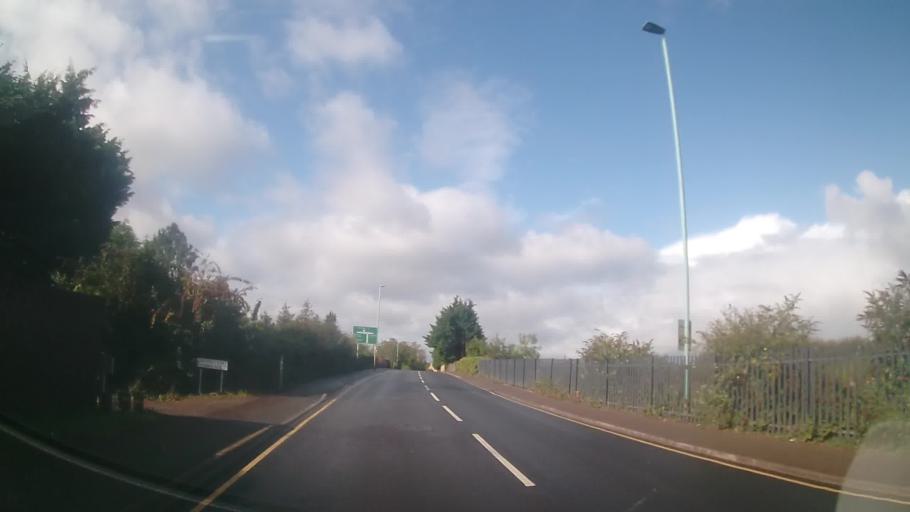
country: GB
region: England
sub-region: Gloucestershire
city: Moreton in Marsh
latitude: 51.9912
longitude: -1.6978
